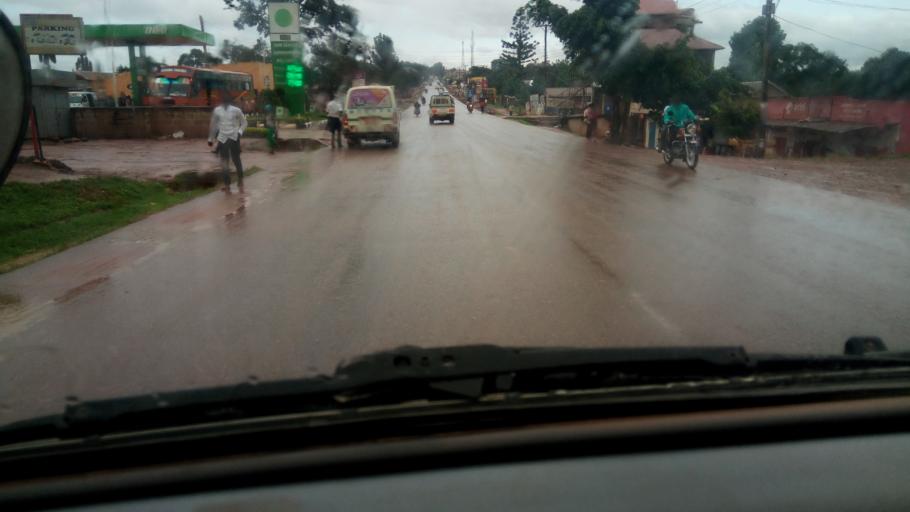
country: UG
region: Central Region
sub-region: Wakiso District
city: Wakiso
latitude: 0.3764
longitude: 32.5203
